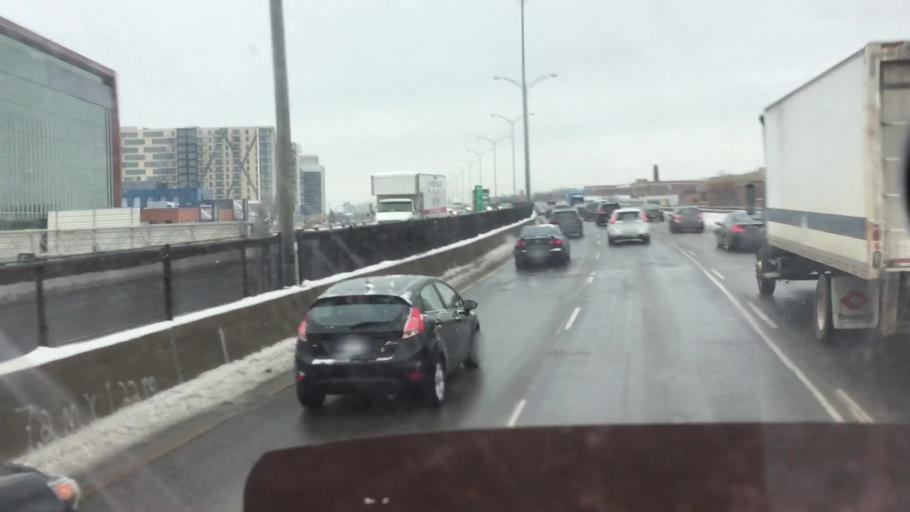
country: CA
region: Quebec
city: Mont-Royal
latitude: 45.5505
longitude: -73.6296
